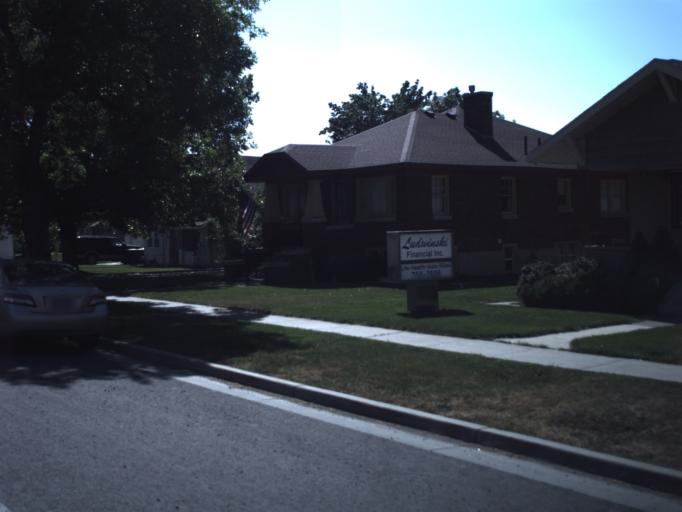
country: US
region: Utah
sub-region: Cache County
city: Smithfield
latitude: 41.8361
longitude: -111.8328
